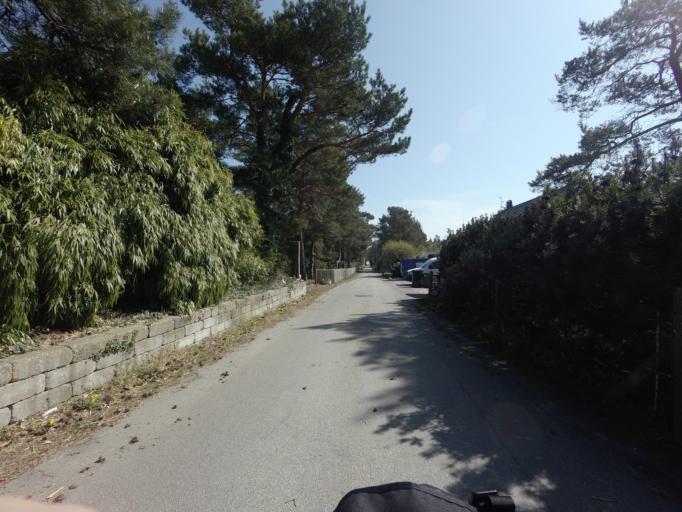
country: SE
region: Skane
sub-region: Vellinge Kommun
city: Hollviken
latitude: 55.4043
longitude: 12.9530
